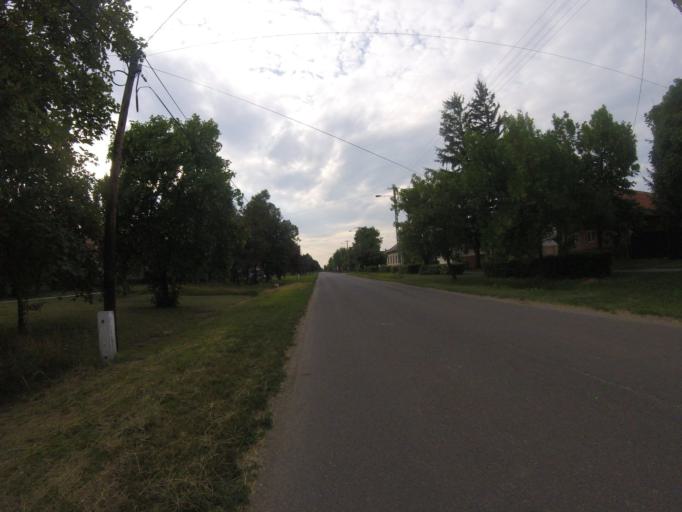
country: HU
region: Heves
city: Tiszanana
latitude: 47.5902
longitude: 20.5942
